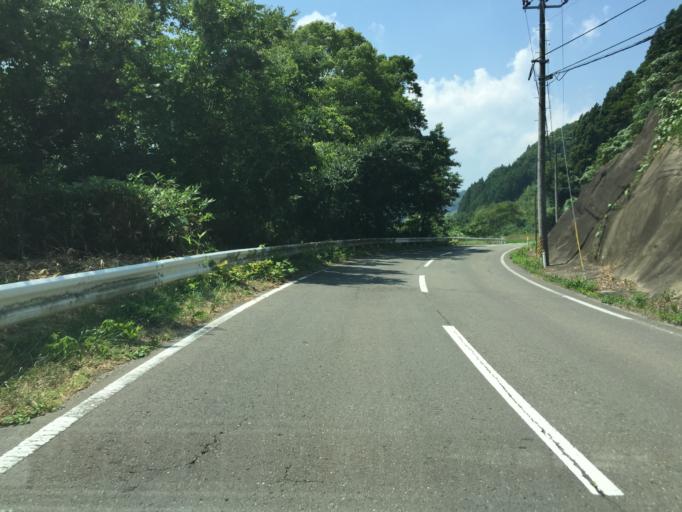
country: JP
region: Miyagi
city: Marumori
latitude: 37.9347
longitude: 140.7126
